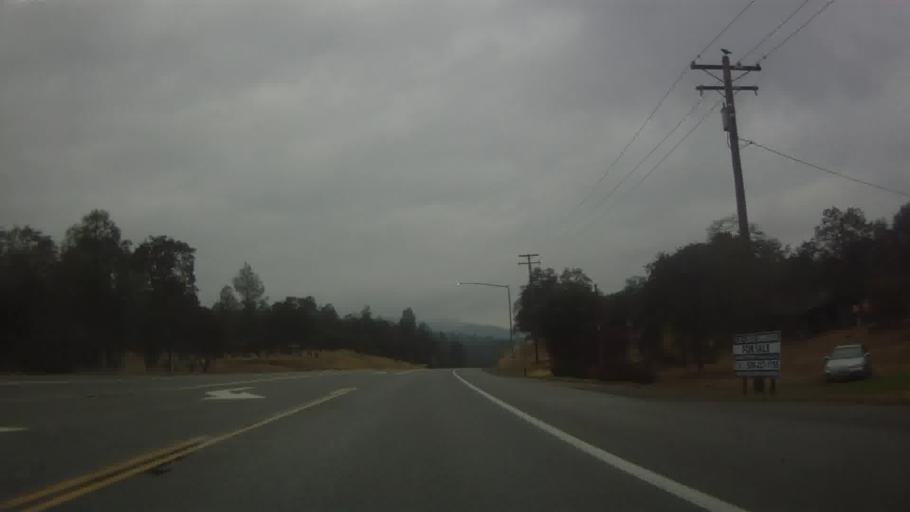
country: US
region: California
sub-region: Shasta County
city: Shasta
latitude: 40.5843
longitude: -122.4458
